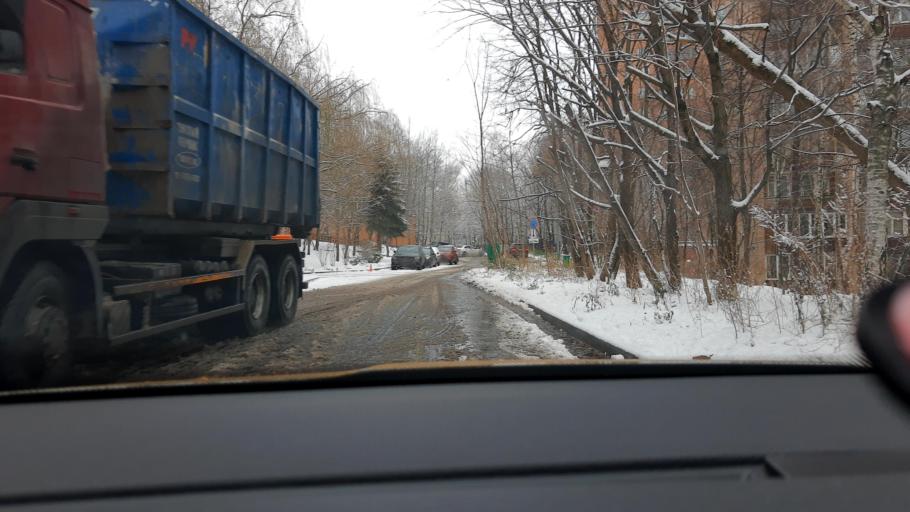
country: RU
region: Moscow
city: Vorob'yovo
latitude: 55.7165
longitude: 37.5261
